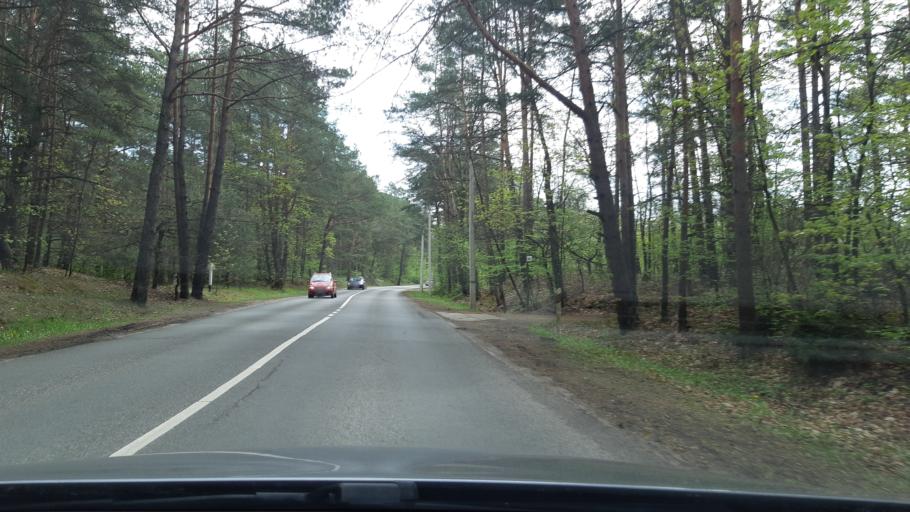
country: LT
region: Kauno apskritis
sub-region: Kauno rajonas
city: Akademija (Kaunas)
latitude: 54.9248
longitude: 23.8335
